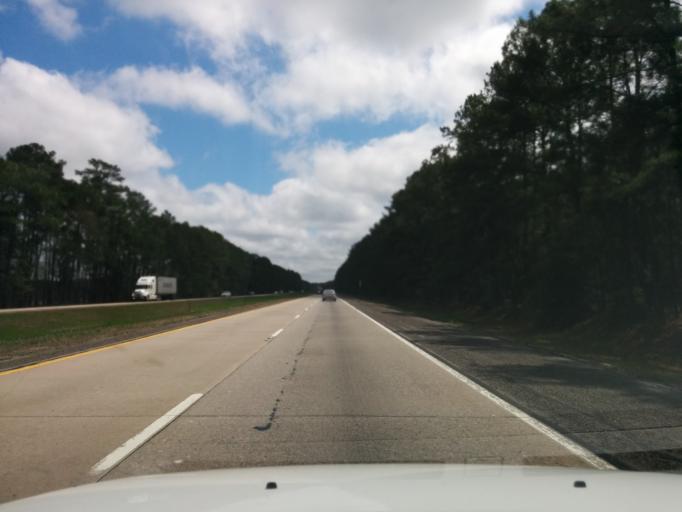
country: US
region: Georgia
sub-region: Chatham County
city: Bloomingdale
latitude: 32.1573
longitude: -81.4309
